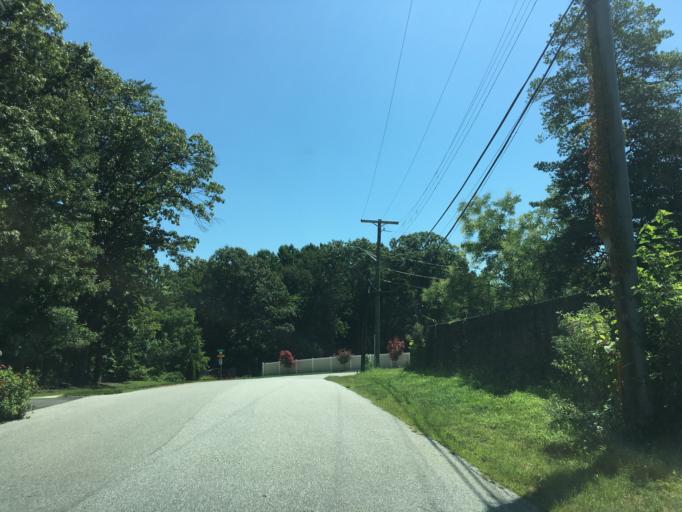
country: US
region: Maryland
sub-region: Anne Arundel County
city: Pasadena
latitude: 39.0922
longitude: -76.5687
